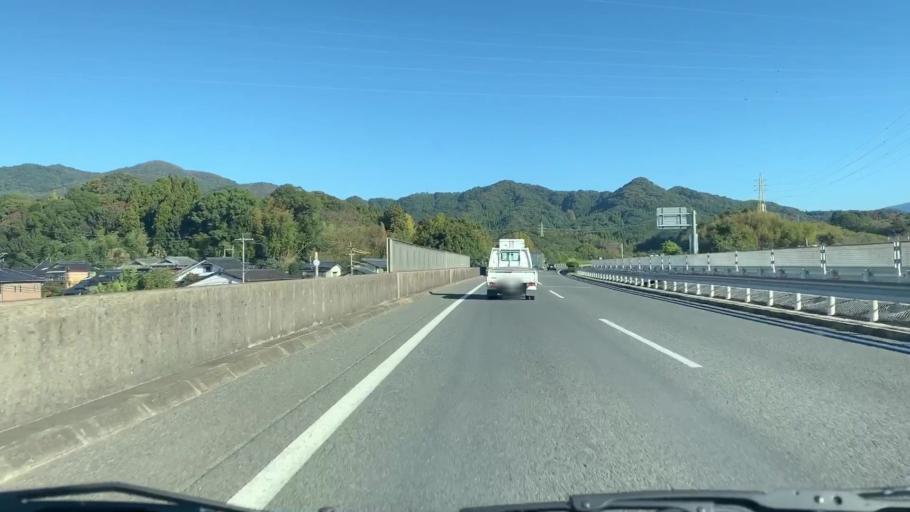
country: JP
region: Saga Prefecture
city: Takeocho-takeo
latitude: 33.2226
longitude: 130.0497
